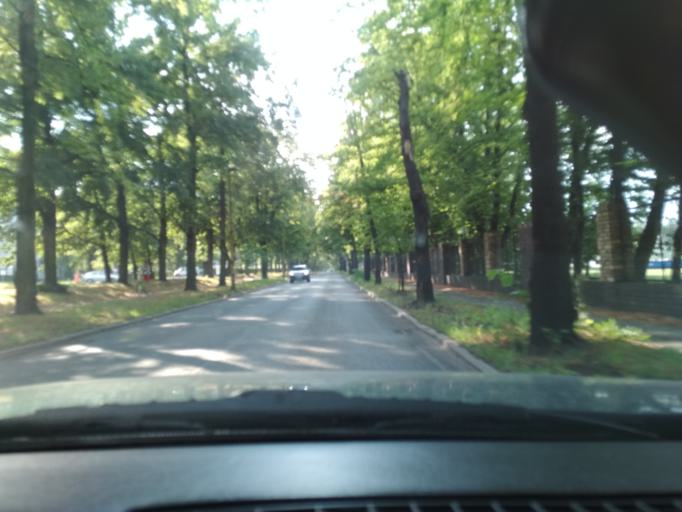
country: PL
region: Silesian Voivodeship
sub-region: Gliwice
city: Gliwice
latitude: 50.2965
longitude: 18.6372
